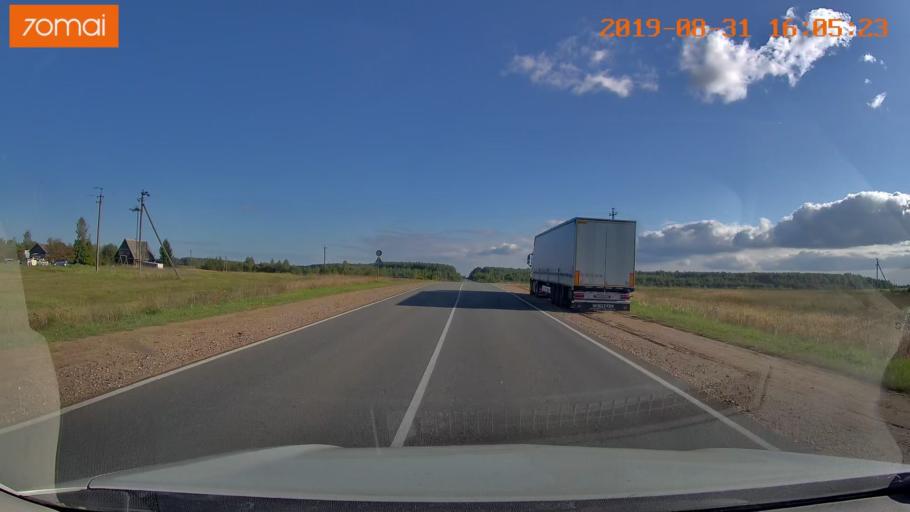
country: RU
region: Kaluga
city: Yukhnov
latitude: 54.6397
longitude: 35.3337
